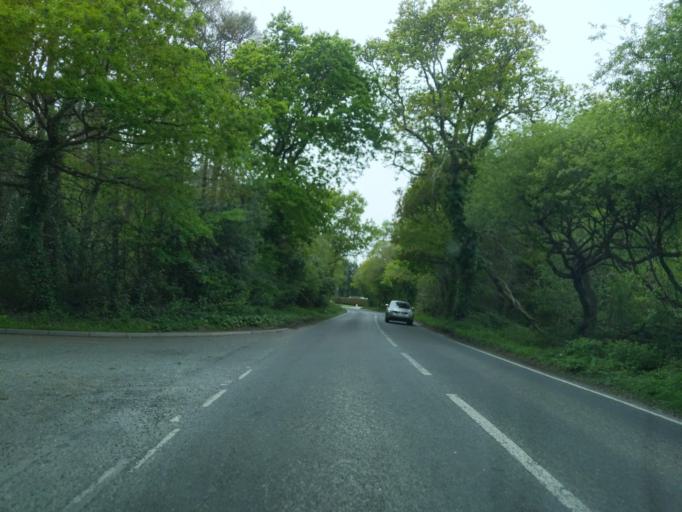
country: GB
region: England
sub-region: Cornwall
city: Par
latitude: 50.3426
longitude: -4.7154
